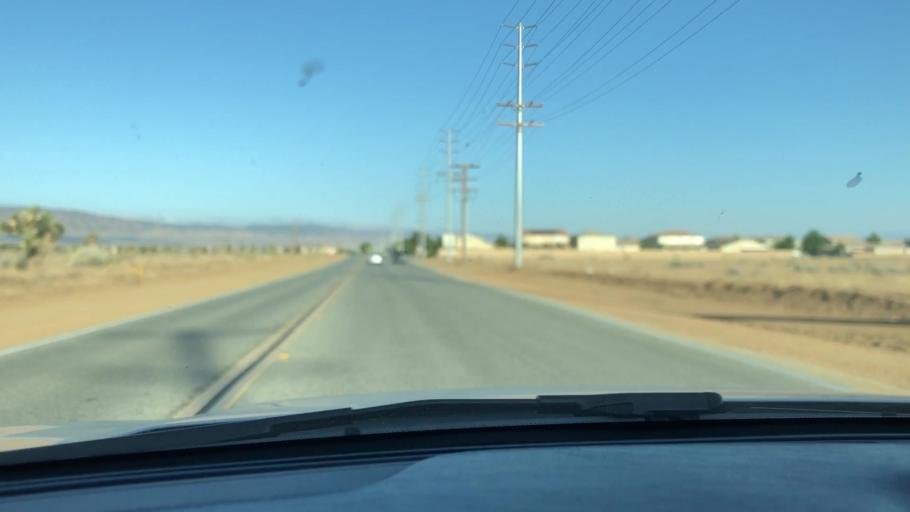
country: US
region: California
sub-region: Los Angeles County
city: Quartz Hill
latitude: 34.6748
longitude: -118.2290
